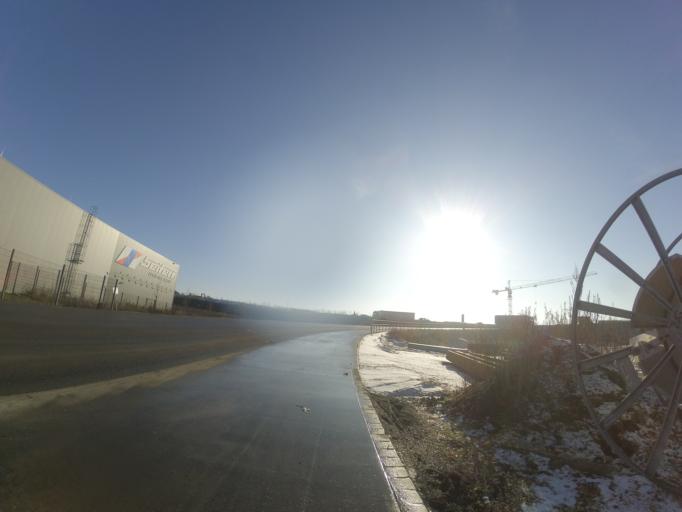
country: DE
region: Baden-Wuerttemberg
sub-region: Tuebingen Region
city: Beimerstetten
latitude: 48.4582
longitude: 9.9773
